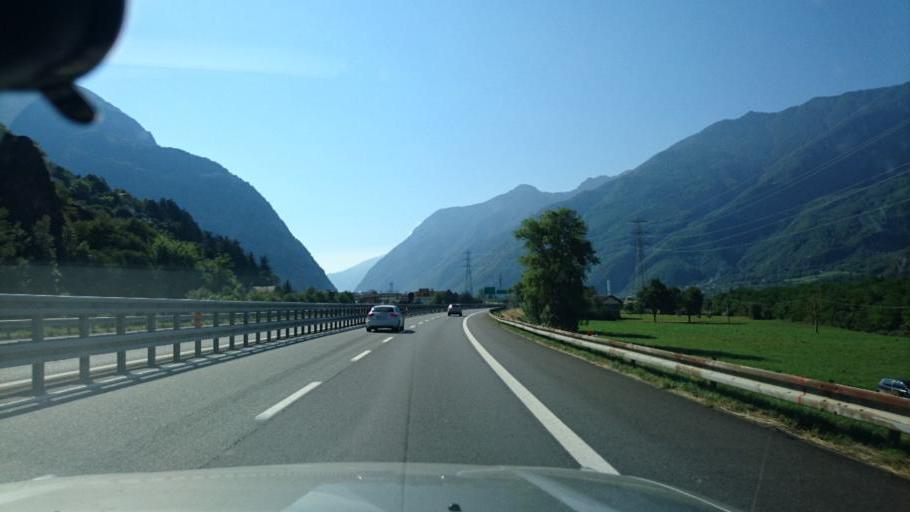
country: IT
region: Aosta Valley
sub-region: Valle d'Aosta
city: Verres
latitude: 45.6744
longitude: 7.6814
